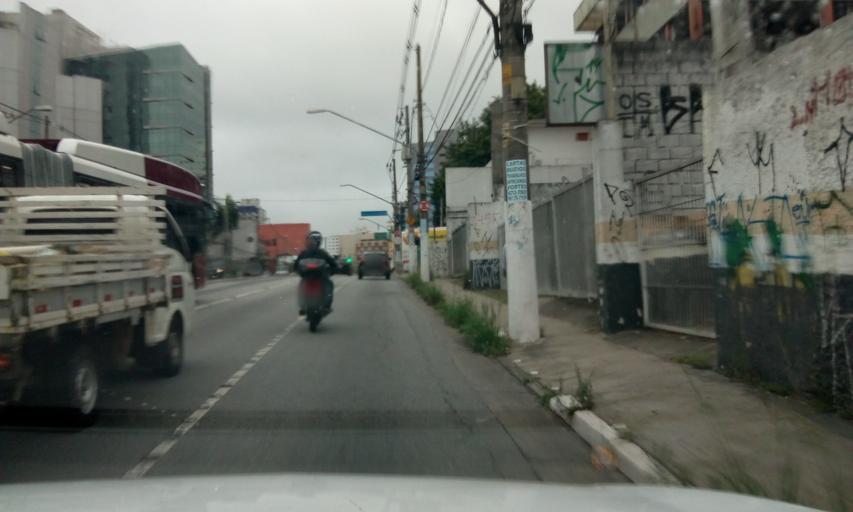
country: BR
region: Sao Paulo
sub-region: Sao Paulo
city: Sao Paulo
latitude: -23.6061
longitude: -46.6756
